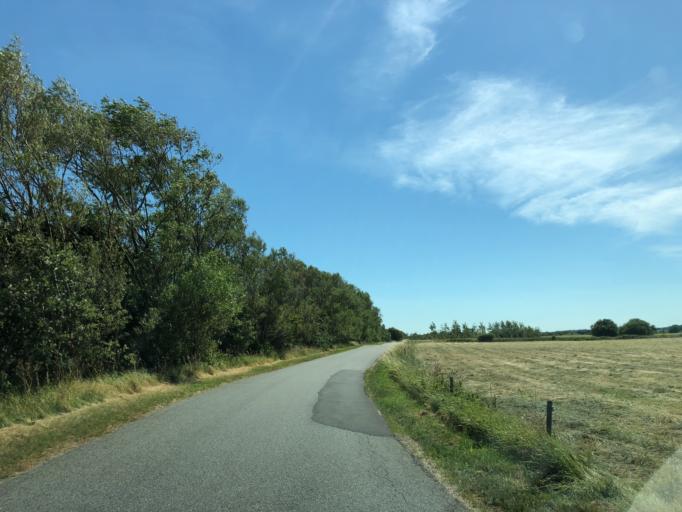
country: DK
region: Central Jutland
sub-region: Skive Kommune
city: Skive
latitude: 56.4688
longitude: 8.9928
